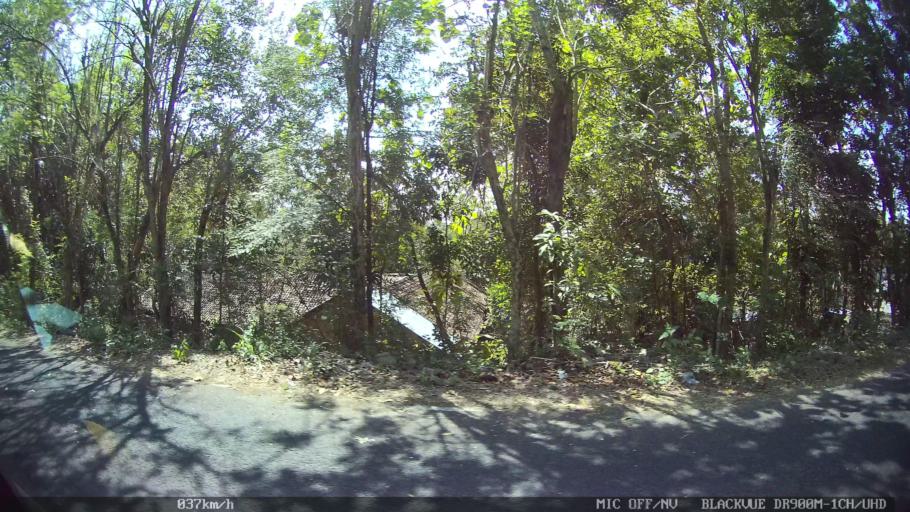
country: ID
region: Daerah Istimewa Yogyakarta
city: Pundong
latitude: -7.9586
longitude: 110.3605
